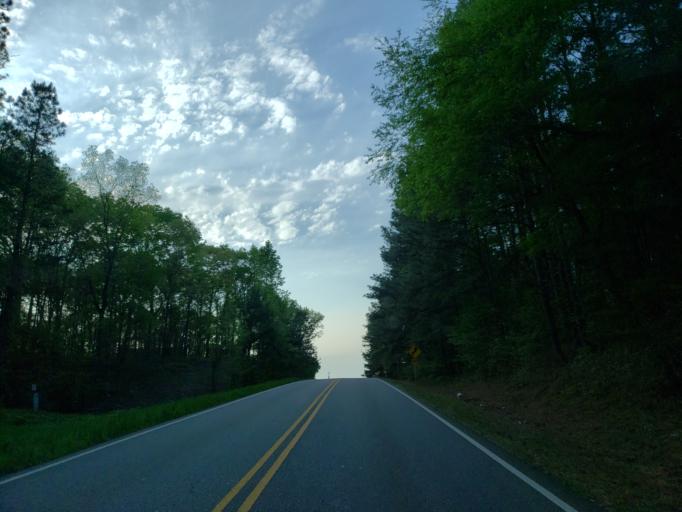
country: US
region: Georgia
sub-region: Cherokee County
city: Ball Ground
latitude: 34.2775
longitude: -84.3741
